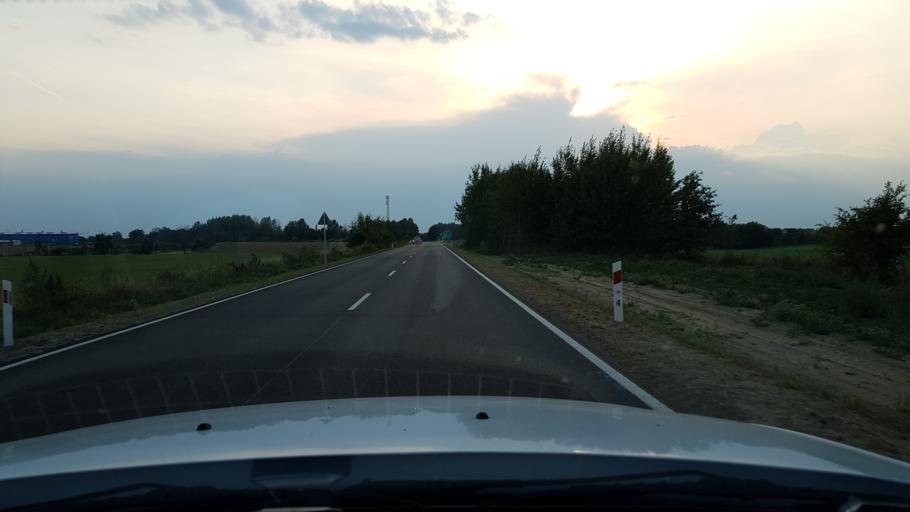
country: PL
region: West Pomeranian Voivodeship
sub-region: Powiat stargardzki
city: Stara Dabrowa
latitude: 53.4339
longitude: 15.0821
